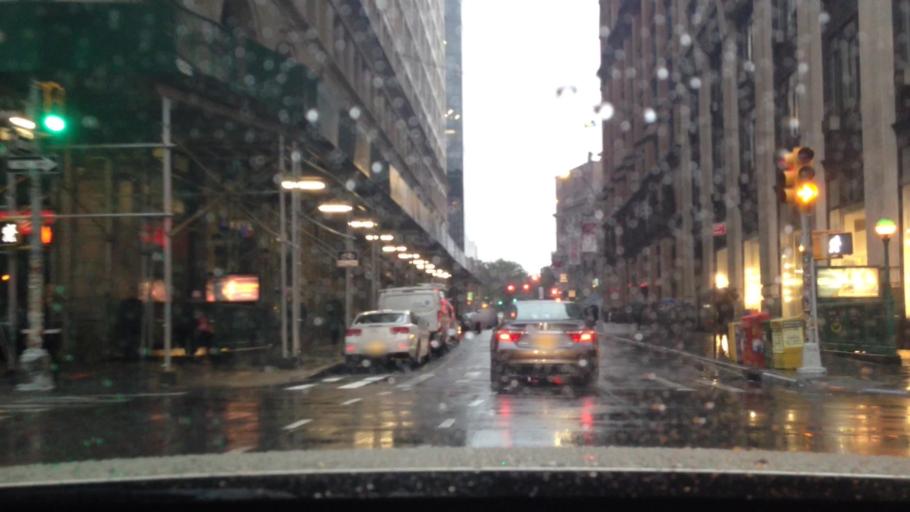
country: US
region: New York
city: New York City
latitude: 40.7307
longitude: -73.9926
